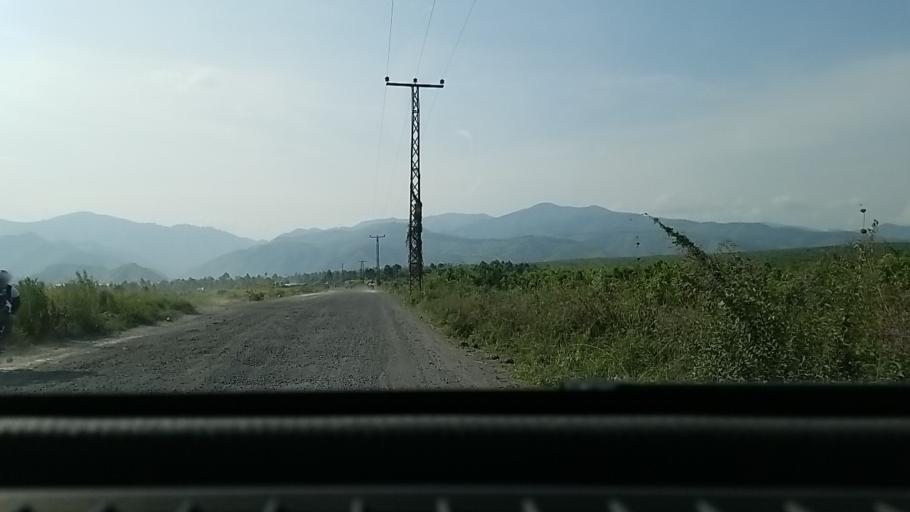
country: CD
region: Nord Kivu
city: Sake
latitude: -1.5805
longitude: 29.0795
